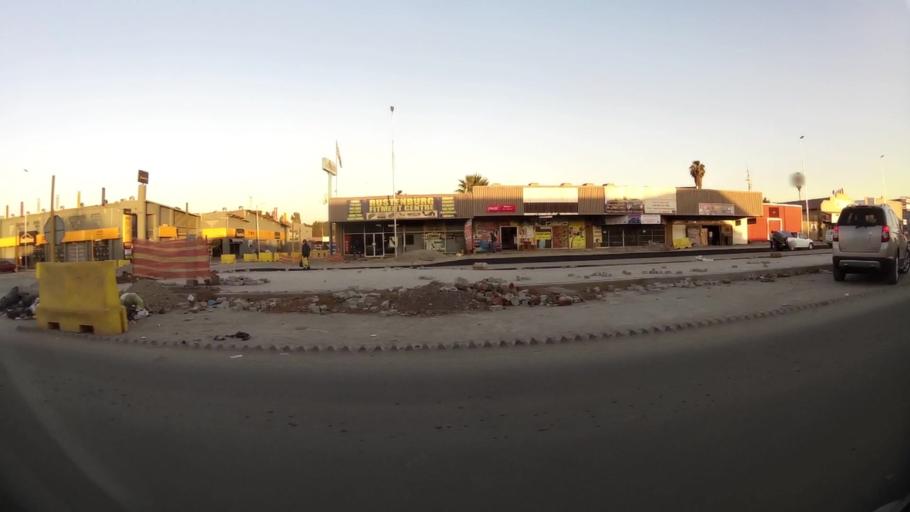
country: ZA
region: North-West
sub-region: Bojanala Platinum District Municipality
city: Rustenburg
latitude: -25.6643
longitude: 27.2433
